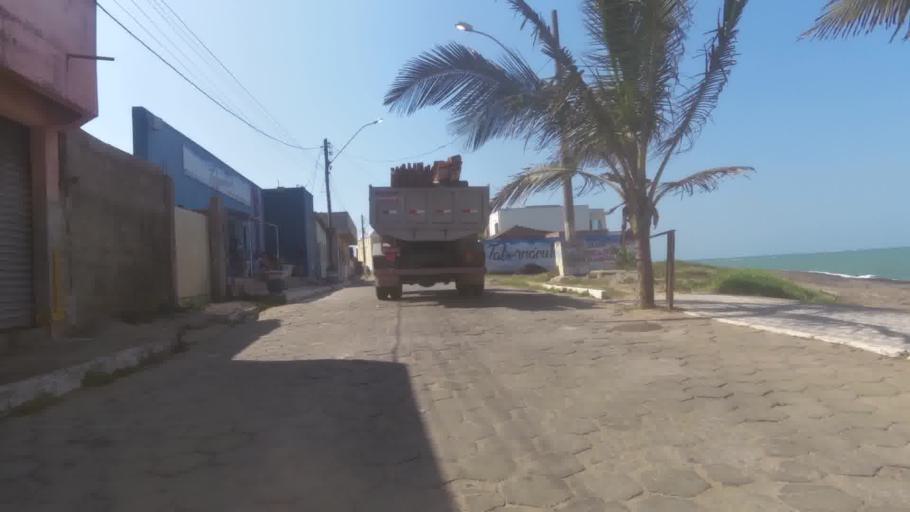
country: BR
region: Espirito Santo
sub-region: Itapemirim
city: Itapemirim
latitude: -21.0097
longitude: -40.8080
